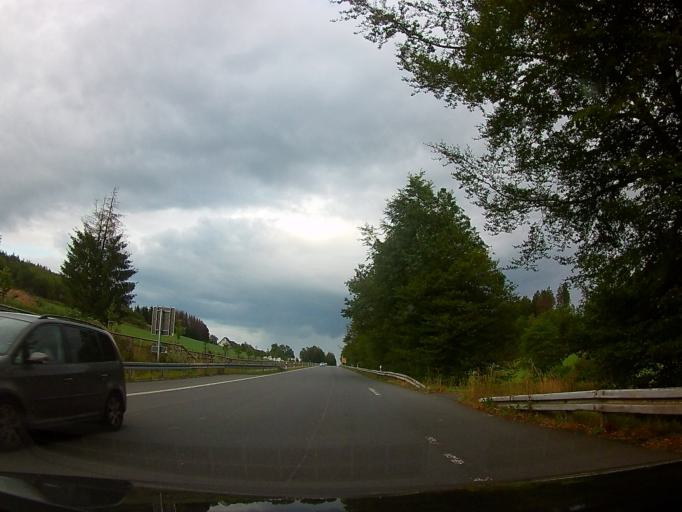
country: DE
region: North Rhine-Westphalia
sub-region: Regierungsbezirk Arnsberg
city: Herscheid
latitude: 51.1152
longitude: 7.7393
